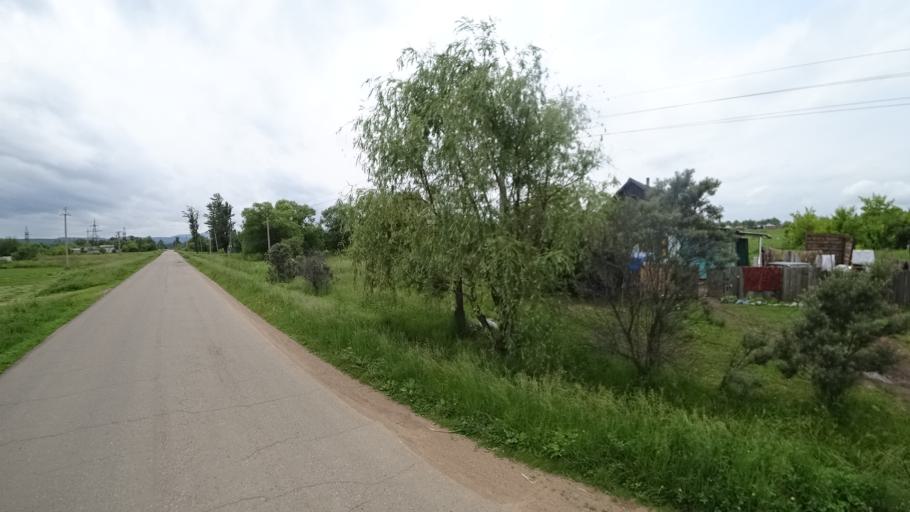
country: RU
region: Primorskiy
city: Novosysoyevka
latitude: 44.2365
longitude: 133.3697
